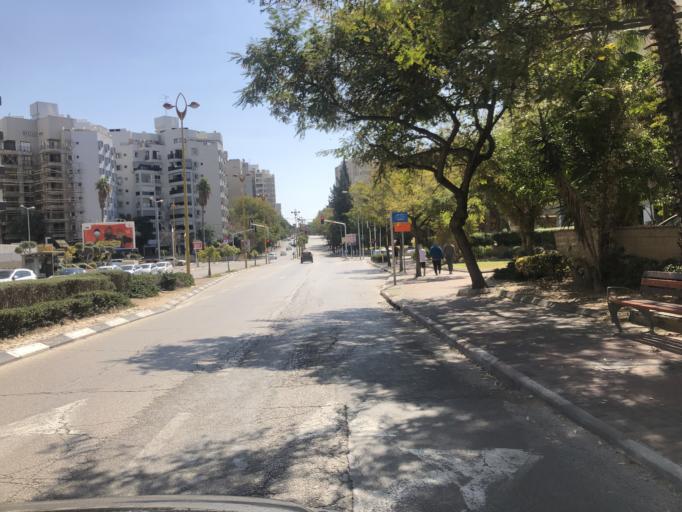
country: IL
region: Tel Aviv
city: Holon
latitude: 32.0019
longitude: 34.7676
